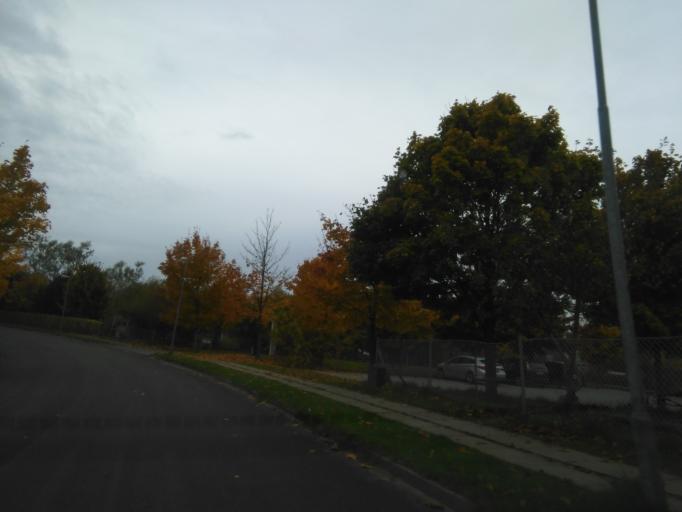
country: DK
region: Central Jutland
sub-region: Arhus Kommune
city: Marslet
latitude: 56.1101
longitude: 10.1760
